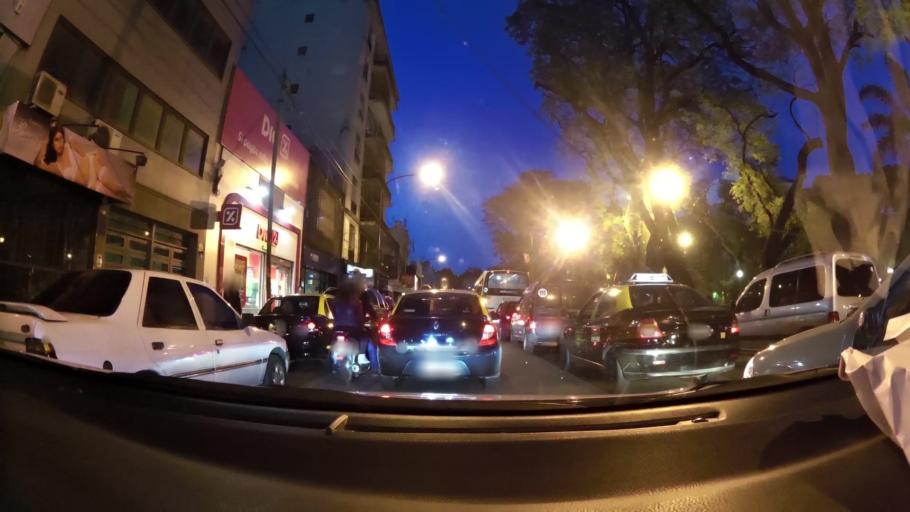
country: AR
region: Buenos Aires F.D.
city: Villa Santa Rita
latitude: -34.6289
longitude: -58.4643
